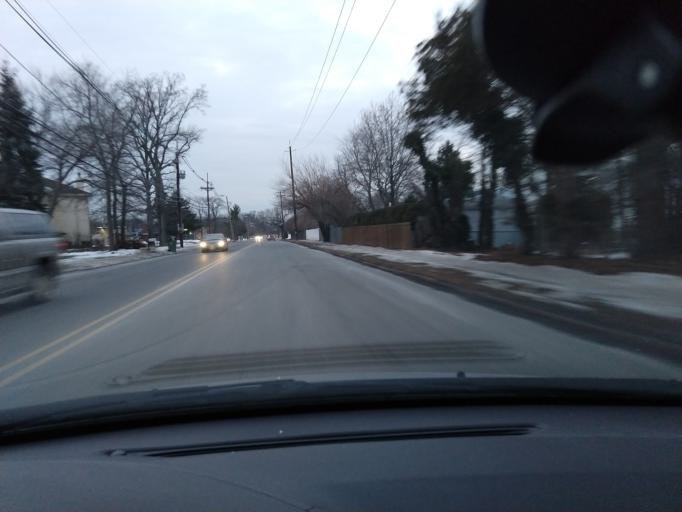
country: US
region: New Jersey
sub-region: Middlesex County
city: Metuchen
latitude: 40.5399
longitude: -74.3808
